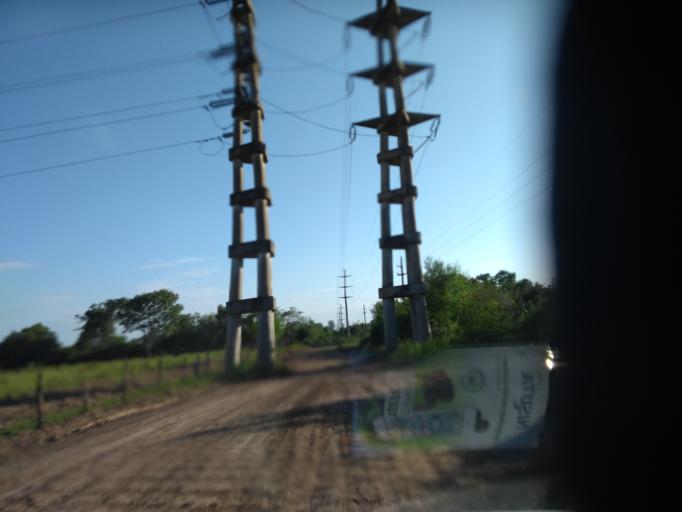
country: AR
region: Chaco
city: Fontana
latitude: -27.4125
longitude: -59.0170
